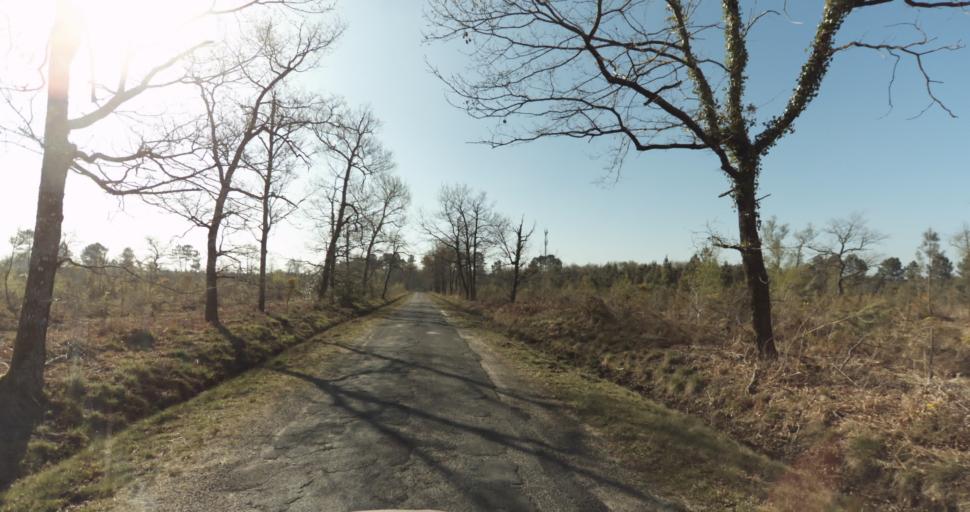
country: FR
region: Aquitaine
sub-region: Departement de la Gironde
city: Martignas-sur-Jalle
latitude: 44.8091
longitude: -0.8506
